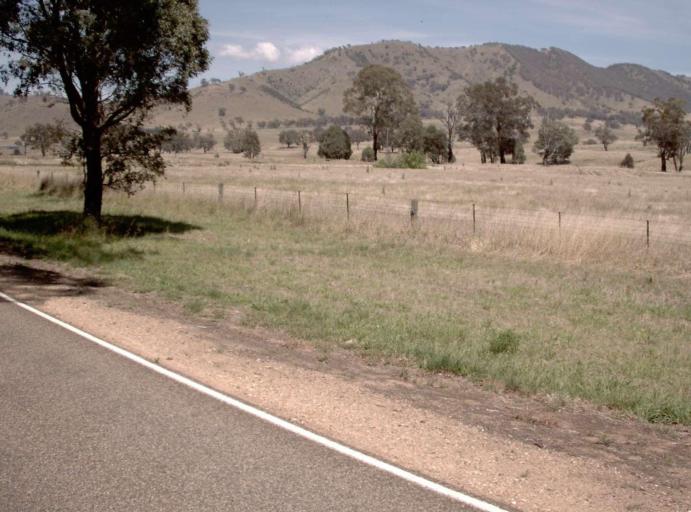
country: AU
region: Victoria
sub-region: East Gippsland
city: Bairnsdale
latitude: -37.2339
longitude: 147.7154
